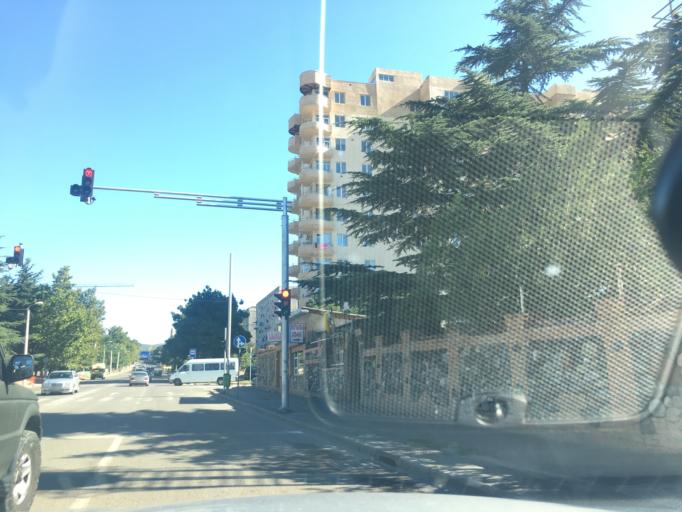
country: GE
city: Zahesi
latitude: 41.7927
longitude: 44.8064
